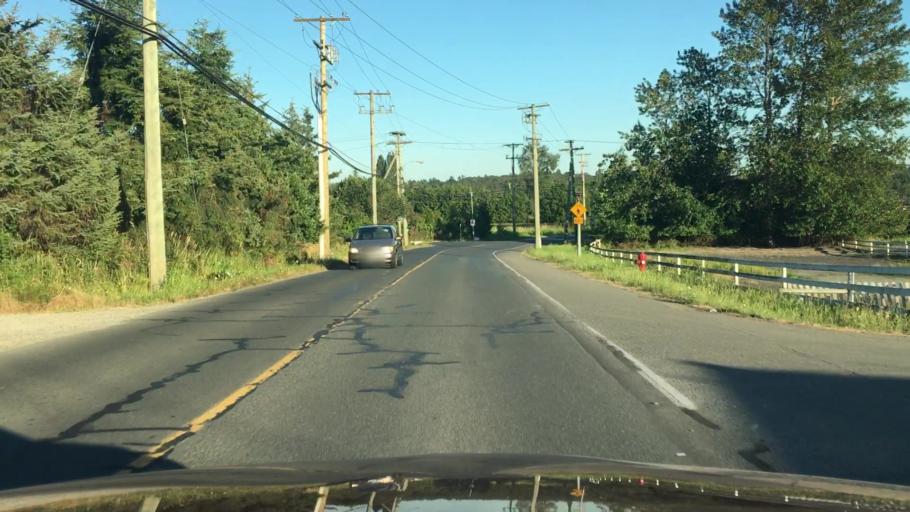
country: CA
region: British Columbia
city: Victoria
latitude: 48.4776
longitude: -123.3535
